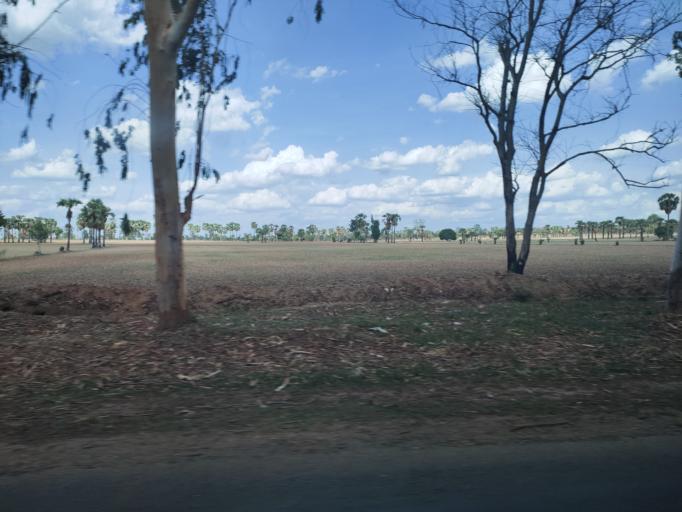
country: MM
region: Magway
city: Magway
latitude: 20.2166
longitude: 95.0176
